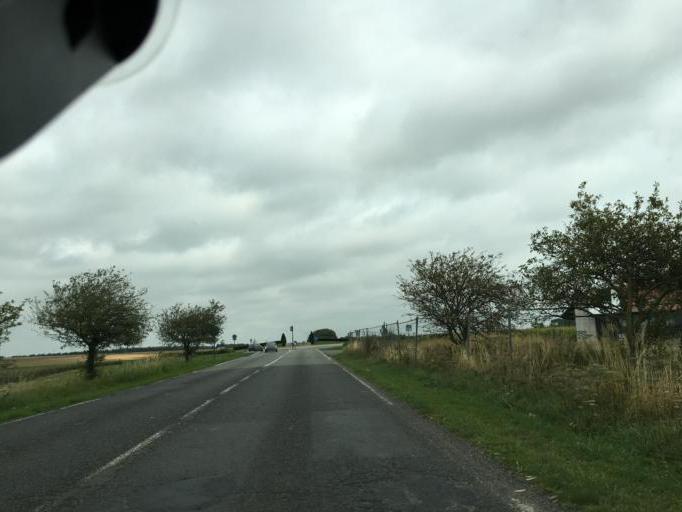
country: FR
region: Nord-Pas-de-Calais
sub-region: Departement du Pas-de-Calais
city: Saint-Pol-sur-Ternoise
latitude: 50.3897
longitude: 2.3516
